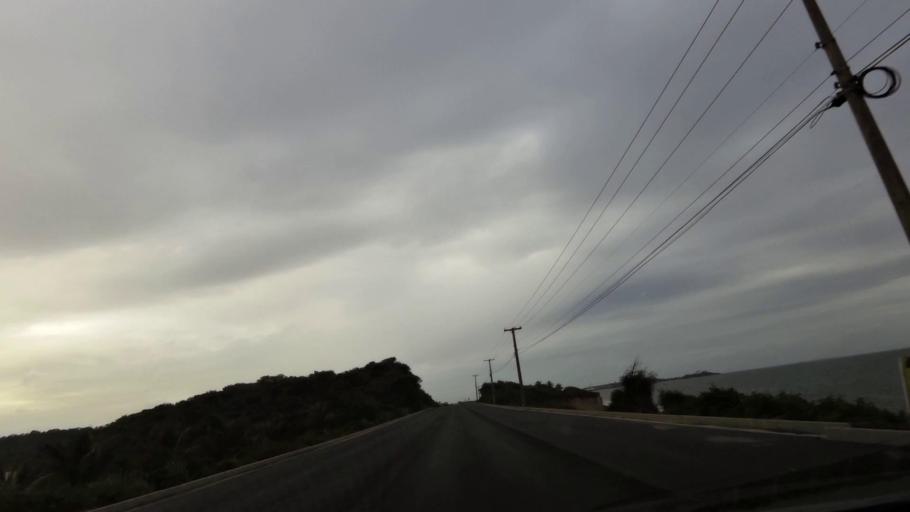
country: BR
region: Espirito Santo
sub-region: Guarapari
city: Guarapari
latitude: -20.7614
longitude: -40.5687
